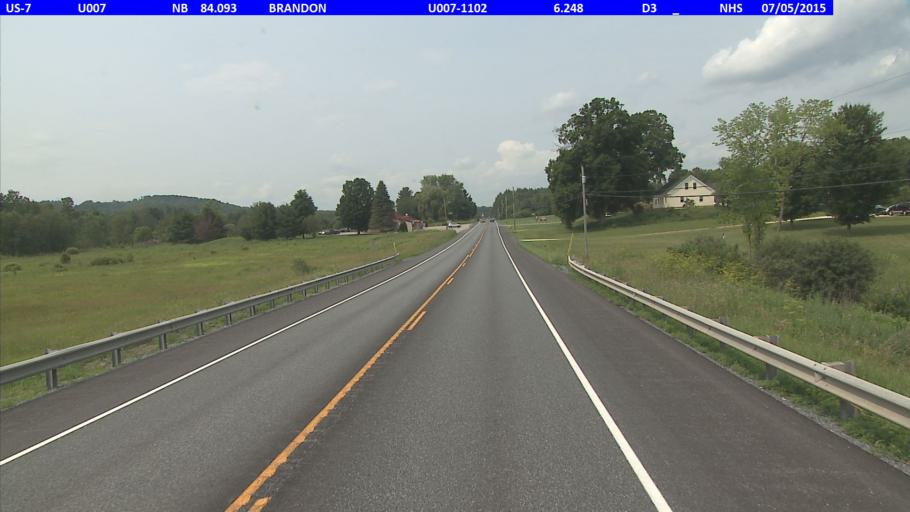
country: US
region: Vermont
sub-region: Rutland County
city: Brandon
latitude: 43.8273
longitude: -73.1047
